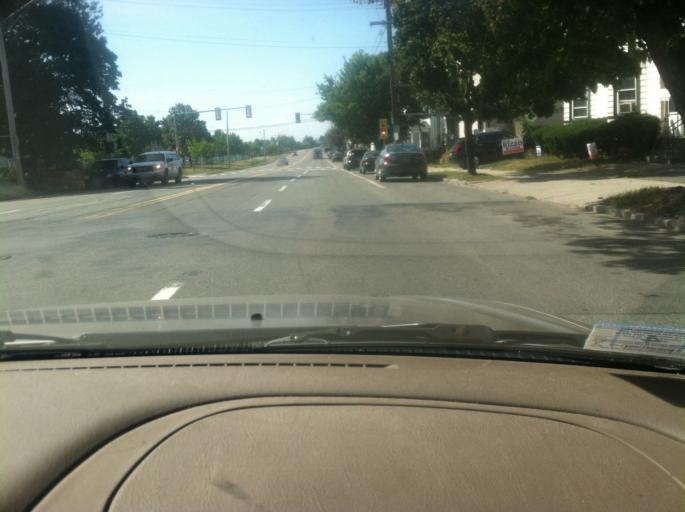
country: US
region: Massachusetts
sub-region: Suffolk County
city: Revere
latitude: 42.3967
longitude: -70.9923
